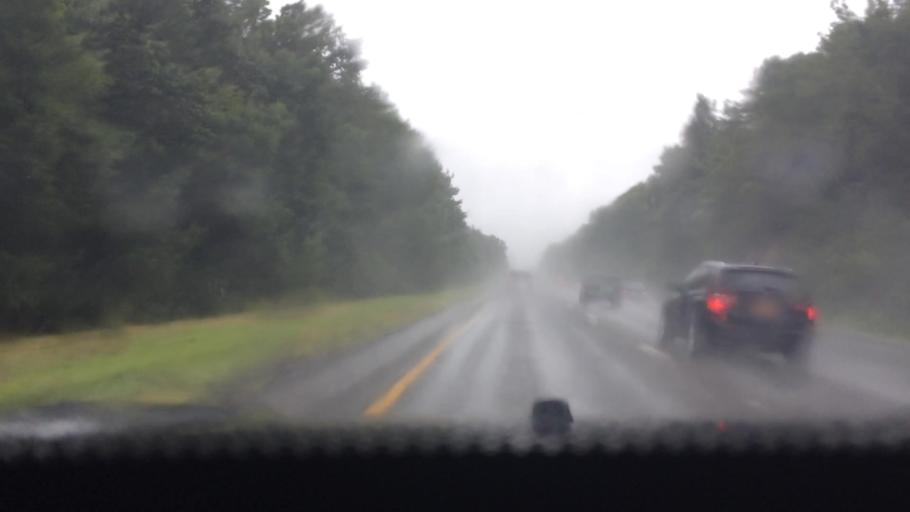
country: US
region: Massachusetts
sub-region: Worcester County
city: Harvard
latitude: 42.4989
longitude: -71.5335
